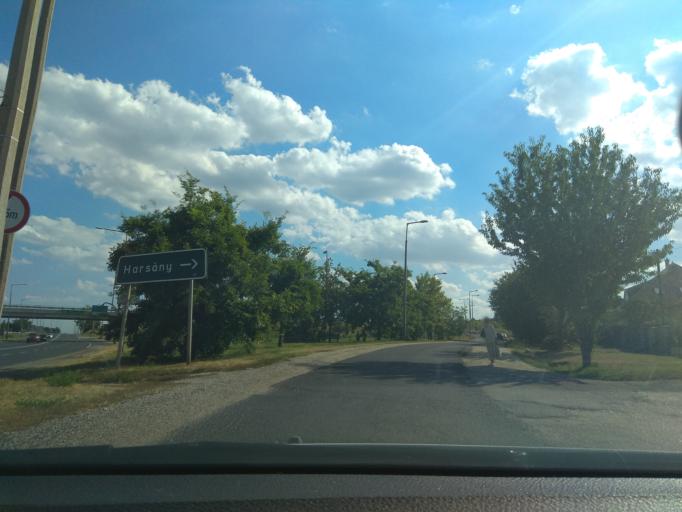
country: HU
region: Borsod-Abauj-Zemplen
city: Miskolc
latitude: 48.0534
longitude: 20.7981
